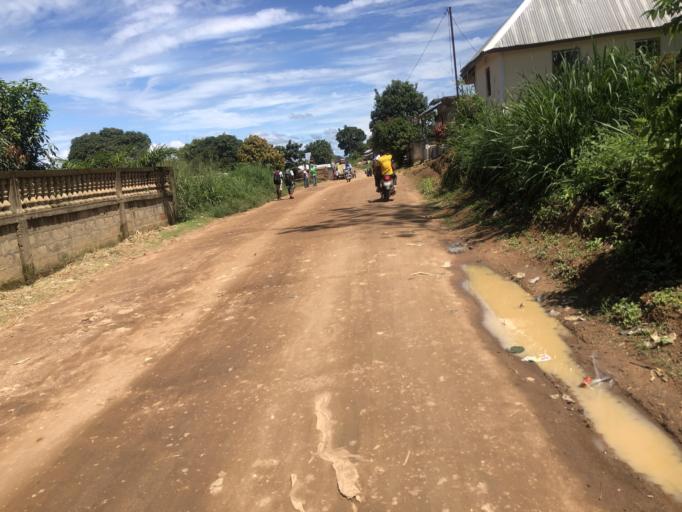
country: SL
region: Eastern Province
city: Koidu
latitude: 8.6405
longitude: -10.9569
